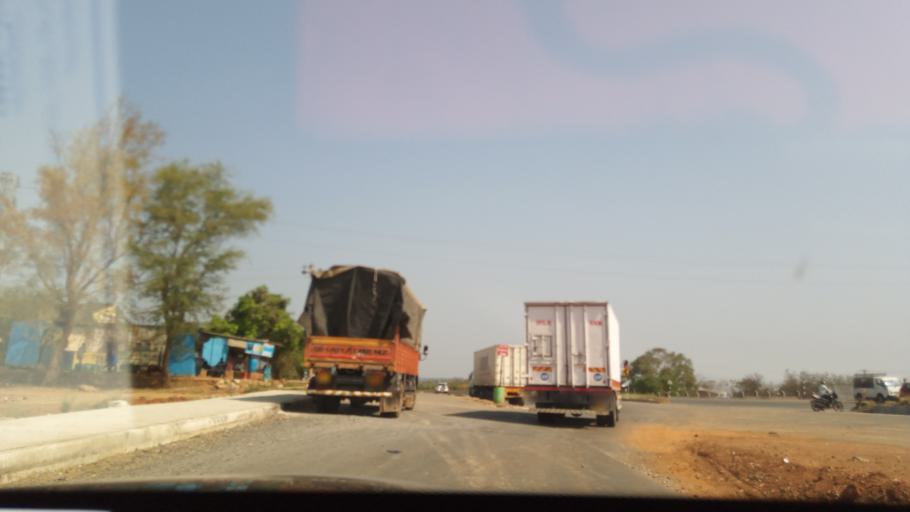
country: IN
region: Karnataka
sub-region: Dharwad
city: Hubli
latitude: 15.2521
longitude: 75.1454
